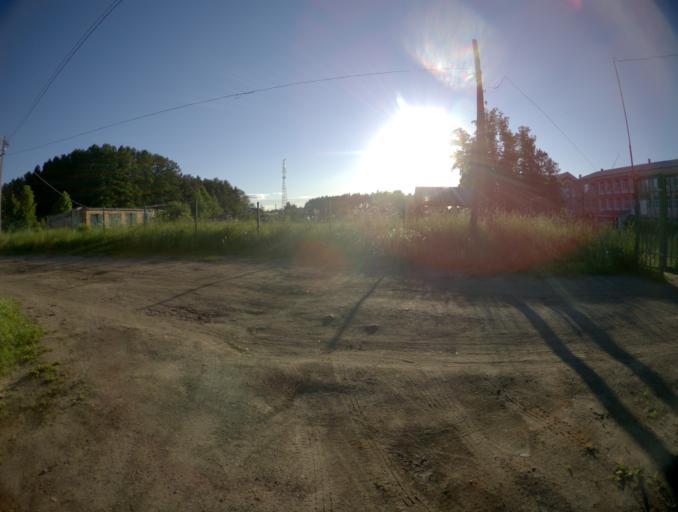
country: RU
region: Ivanovo
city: Lezhnevo
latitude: 56.8653
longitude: 40.7570
